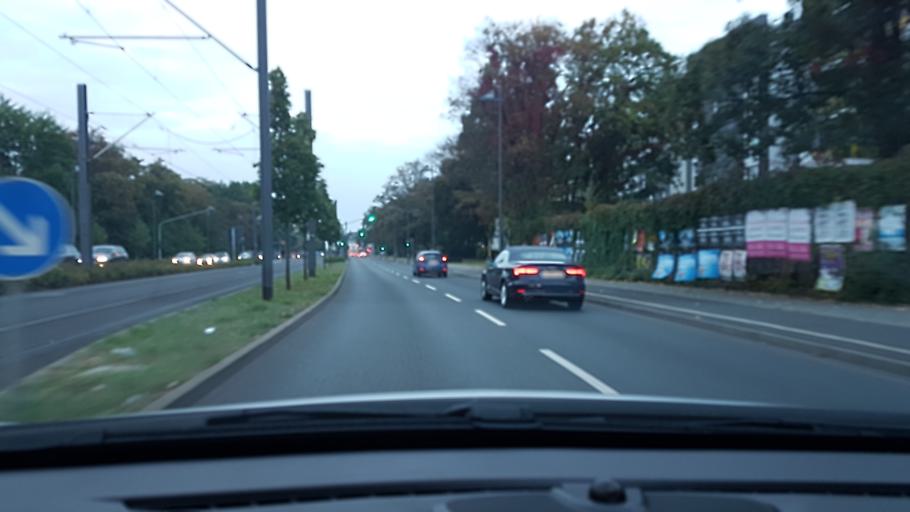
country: DE
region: Hesse
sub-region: Regierungsbezirk Darmstadt
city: Frankfurt am Main
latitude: 50.1430
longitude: 8.7029
